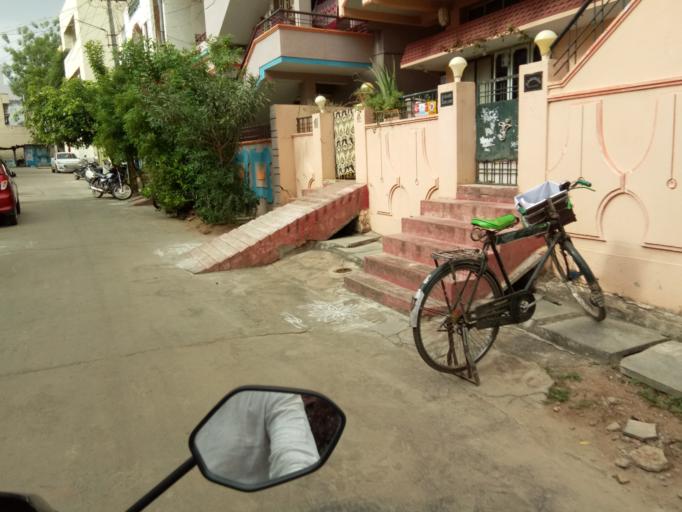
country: IN
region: Telangana
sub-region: Khammam
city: Khammam
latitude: 17.2360
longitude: 80.1470
